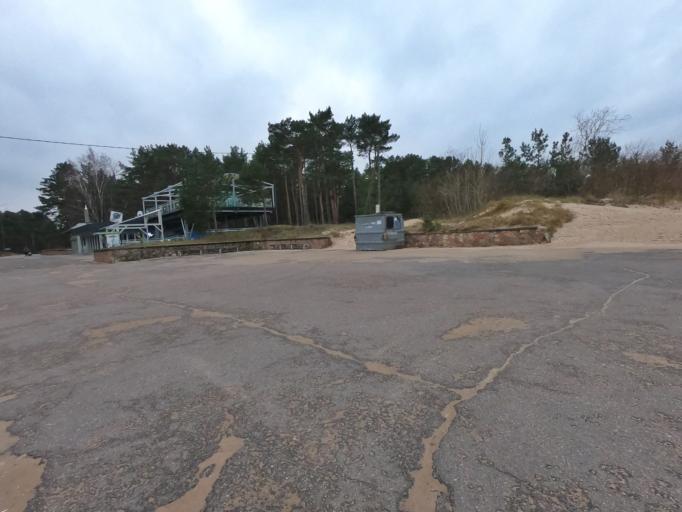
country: LV
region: Riga
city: Bolderaja
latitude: 57.0816
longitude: 24.1075
